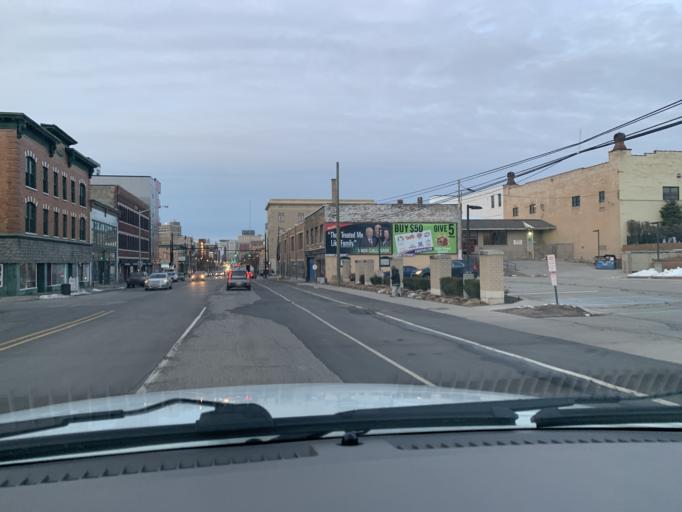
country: US
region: Michigan
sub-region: Kent County
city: Grand Rapids
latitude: 42.9585
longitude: -85.6677
